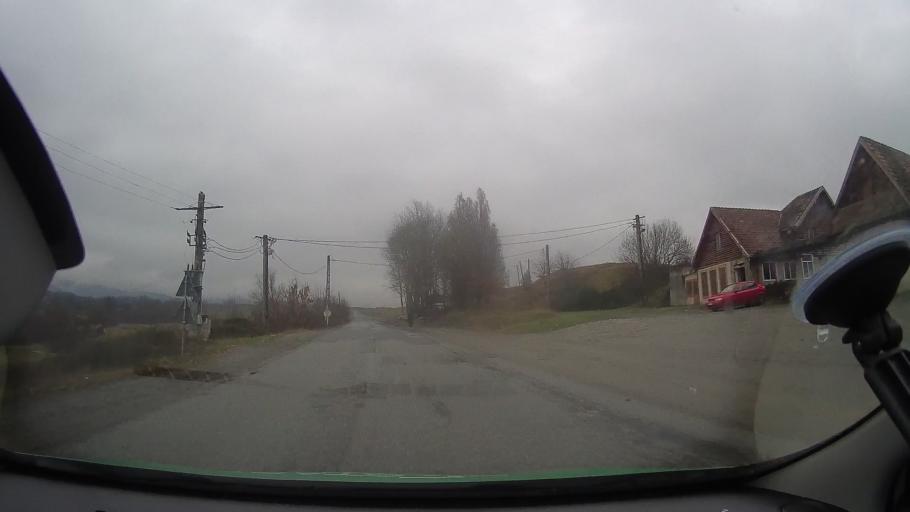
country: RO
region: Arad
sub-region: Comuna Halmagiu
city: Halmagiu
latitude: 46.2823
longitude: 22.5746
